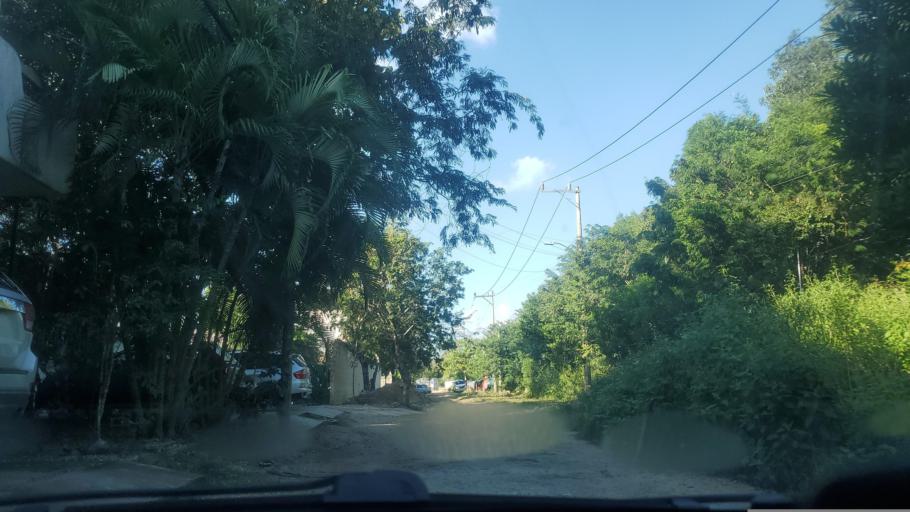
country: MX
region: Quintana Roo
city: Tulum
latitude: 20.2076
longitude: -87.4774
